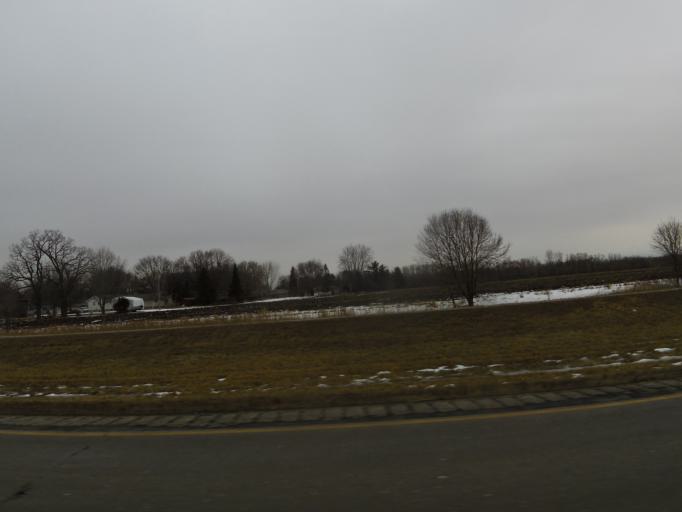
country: US
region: Minnesota
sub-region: Carver County
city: Cologne
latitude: 44.7660
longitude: -93.7762
